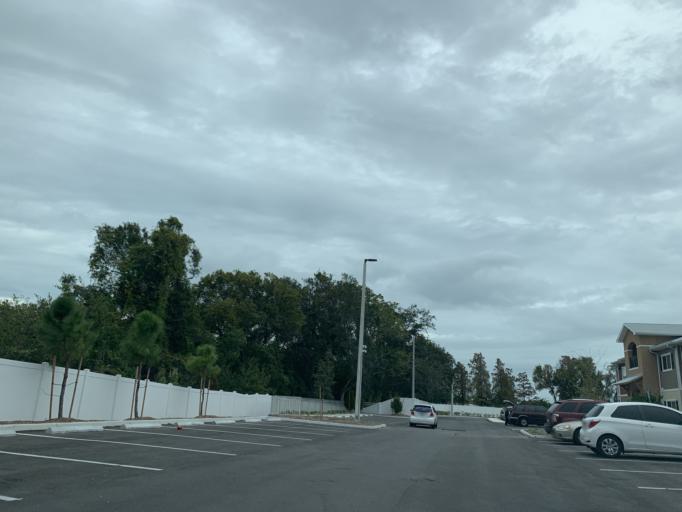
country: US
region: Florida
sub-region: Pinellas County
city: Belleair
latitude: 27.9433
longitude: -82.7956
